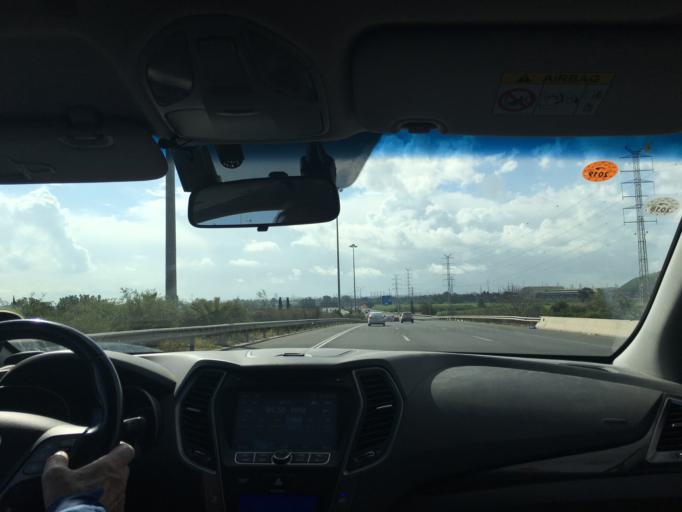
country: IL
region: Tel Aviv
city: Azor
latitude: 32.0375
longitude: 34.8297
